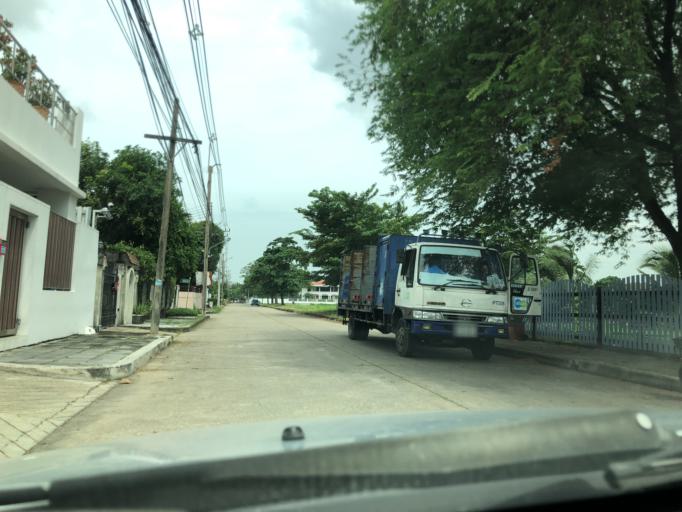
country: TH
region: Nonthaburi
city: Pak Kret
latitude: 13.9185
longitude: 100.5358
